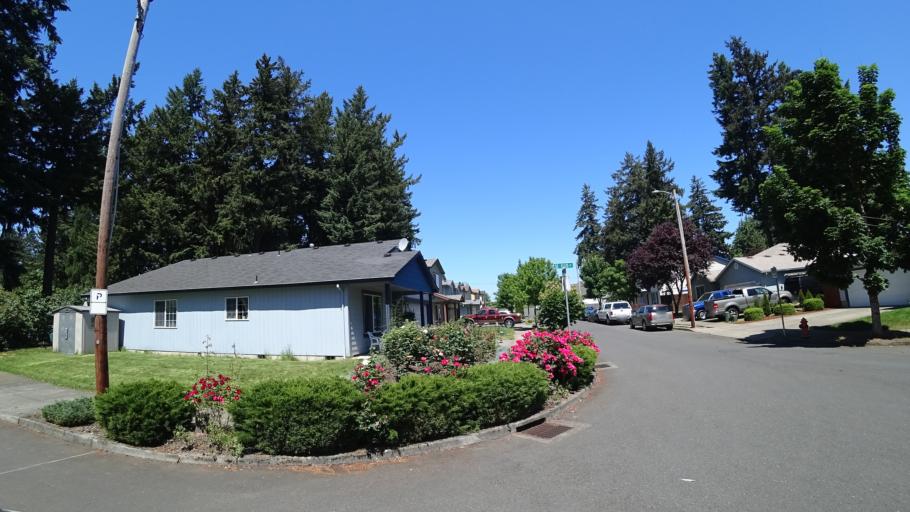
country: US
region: Oregon
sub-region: Clackamas County
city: Happy Valley
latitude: 45.4824
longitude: -122.5263
